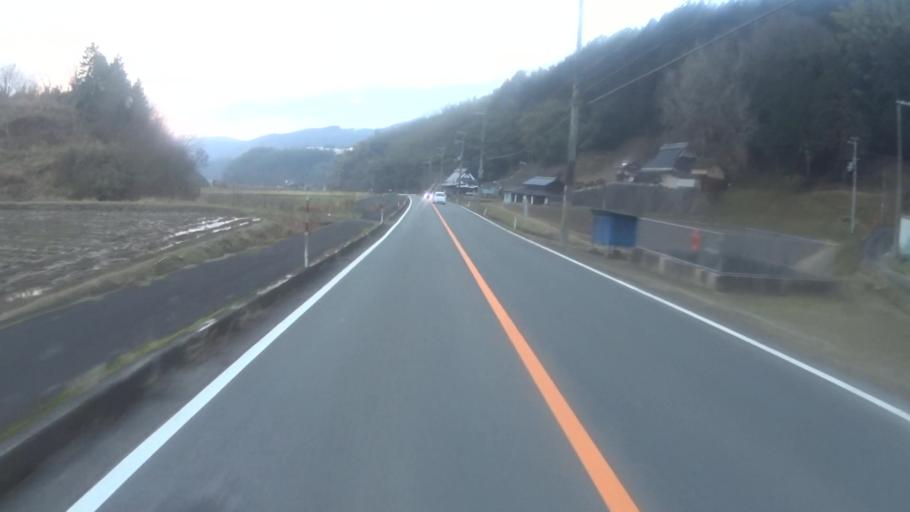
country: JP
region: Kyoto
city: Maizuru
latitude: 35.3396
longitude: 135.3605
